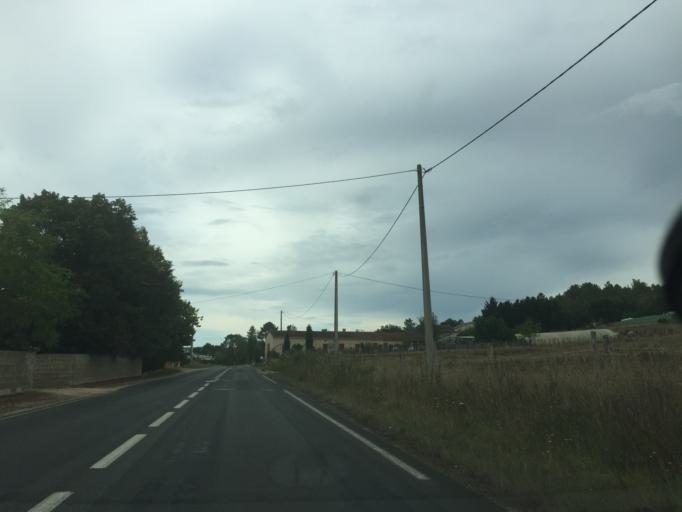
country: FR
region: Aquitaine
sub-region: Departement du Lot-et-Garonne
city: Fumel
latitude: 44.5092
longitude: 0.9493
